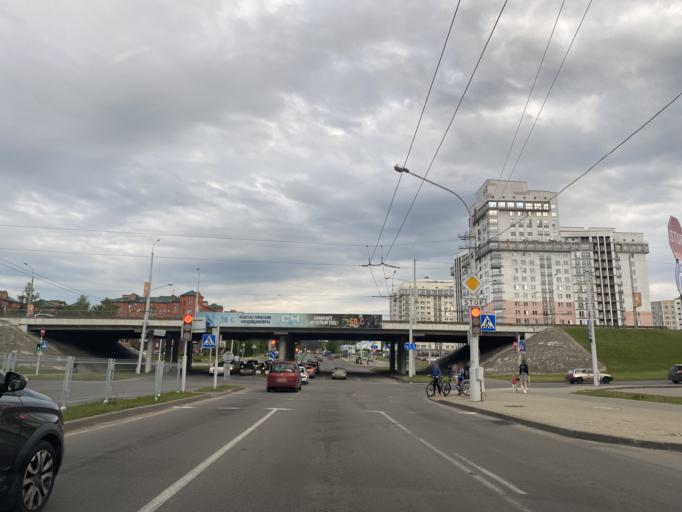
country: BY
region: Minsk
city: Lyeskawka
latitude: 53.9482
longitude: 27.6941
